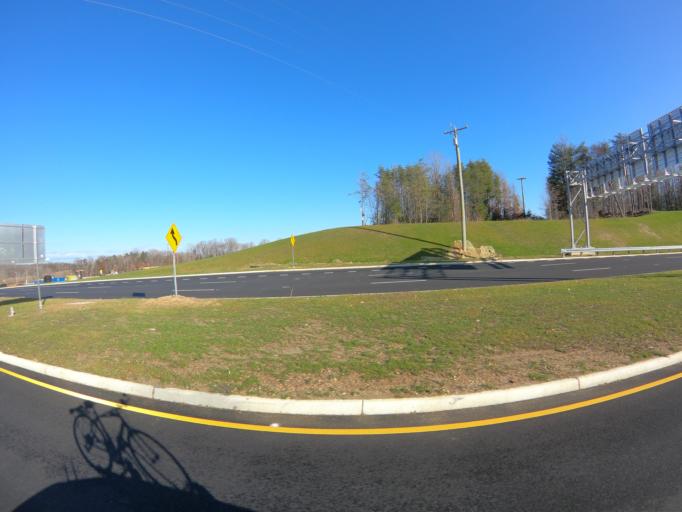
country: US
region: Virginia
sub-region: Stafford County
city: Stafford
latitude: 38.4191
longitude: -77.4195
